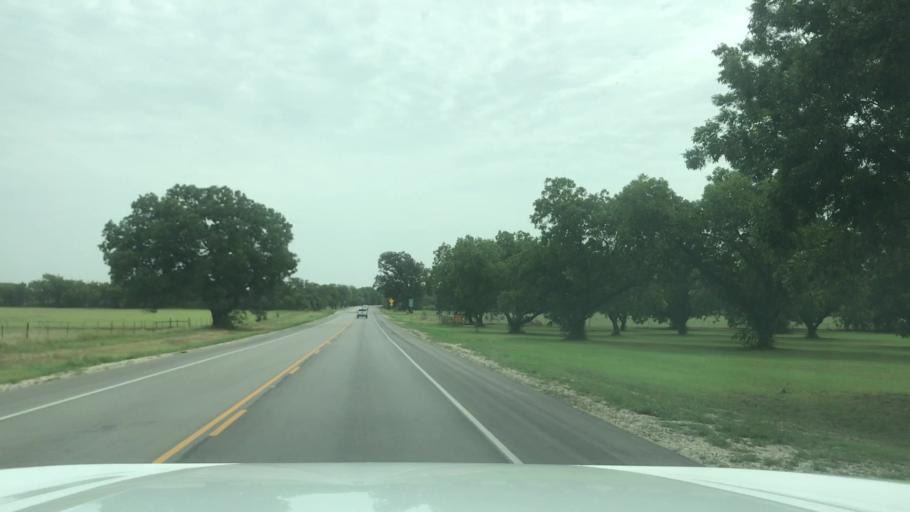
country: US
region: Texas
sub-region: Erath County
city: Dublin
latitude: 32.0912
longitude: -98.2754
